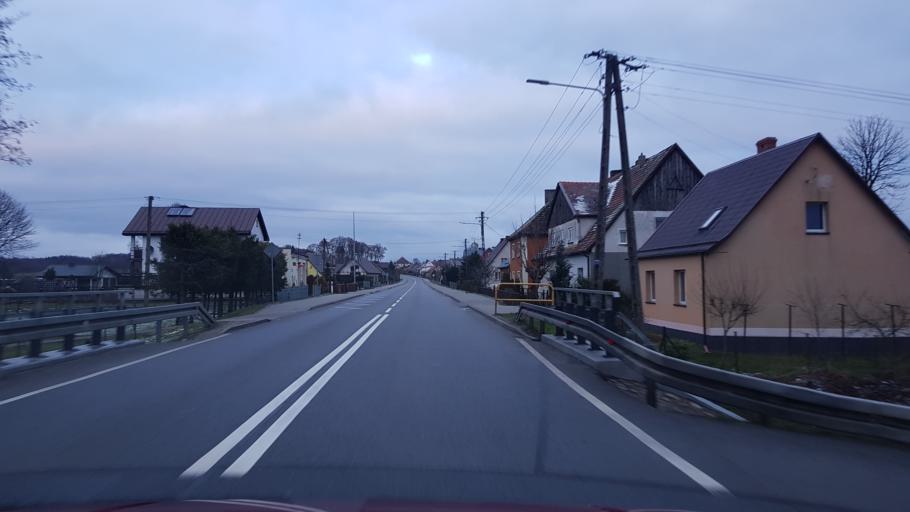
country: PL
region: Pomeranian Voivodeship
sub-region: Powiat bytowski
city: Tuchomie
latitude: 54.0547
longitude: 17.2361
